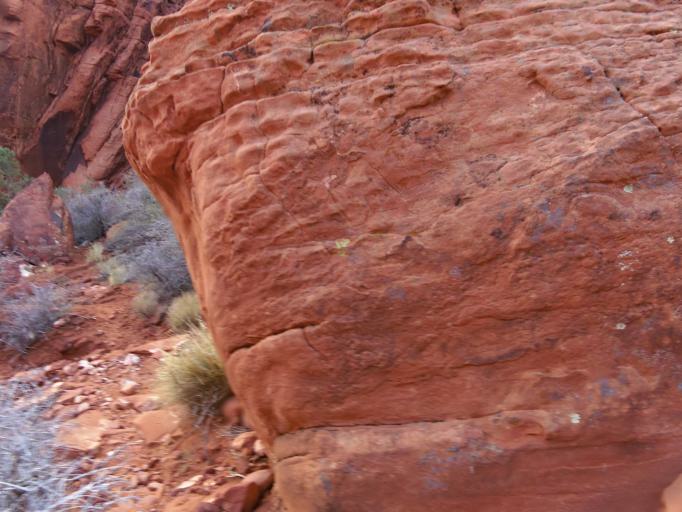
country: US
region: Nevada
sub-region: Clark County
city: Summerlin South
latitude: 36.1533
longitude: -115.4322
